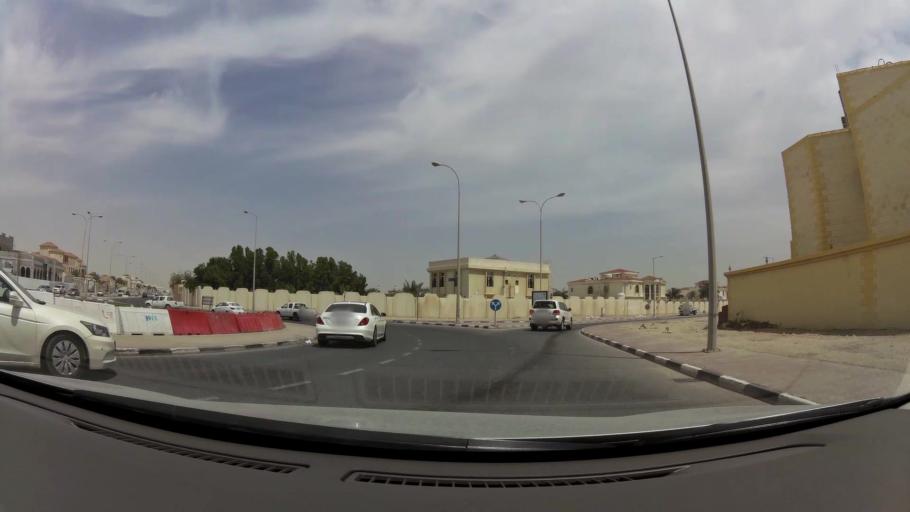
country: QA
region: Baladiyat ar Rayyan
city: Ar Rayyan
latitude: 25.2995
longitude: 51.4121
